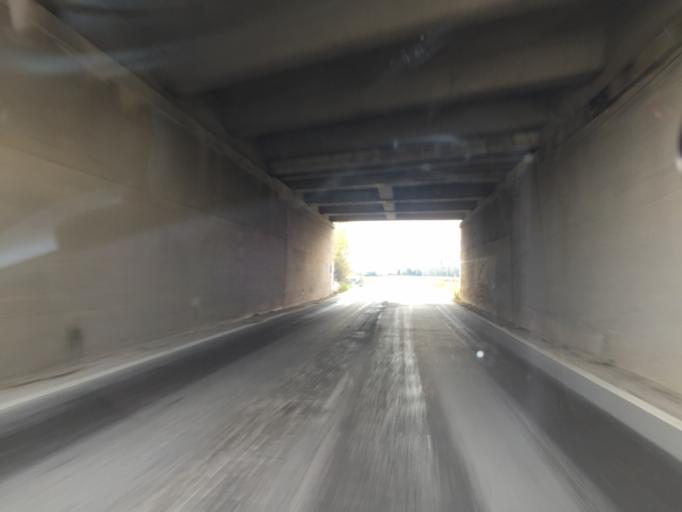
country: FR
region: Provence-Alpes-Cote d'Azur
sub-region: Departement du Vaucluse
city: Bedarrides
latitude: 44.0325
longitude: 4.8859
